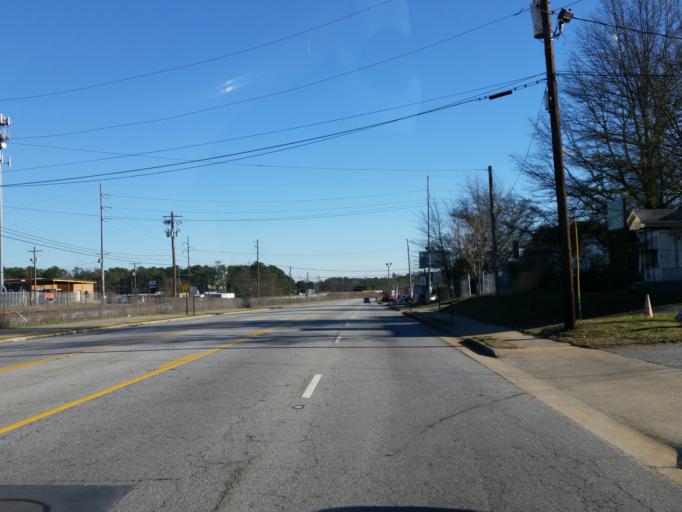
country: US
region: Georgia
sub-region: Cobb County
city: Fair Oaks
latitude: 33.9113
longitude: -84.5335
